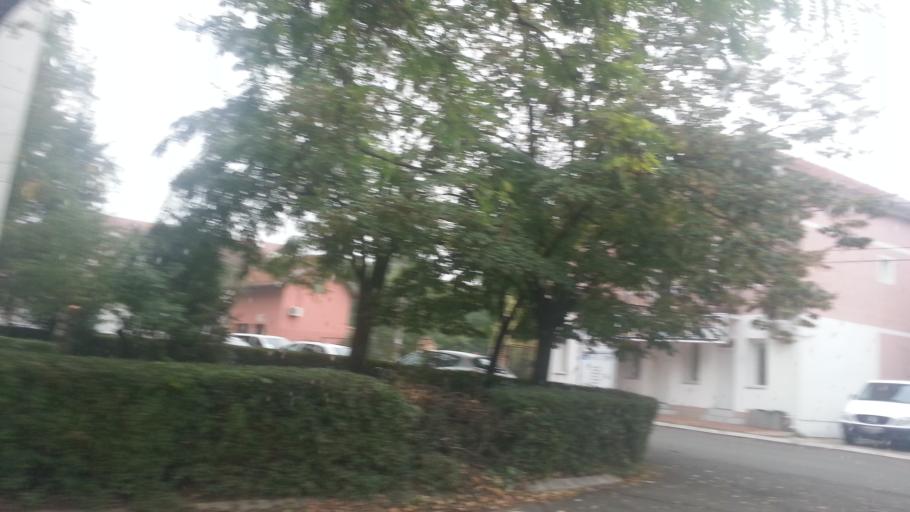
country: RS
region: Central Serbia
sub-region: Belgrade
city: Zemun
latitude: 44.8409
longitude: 20.3898
